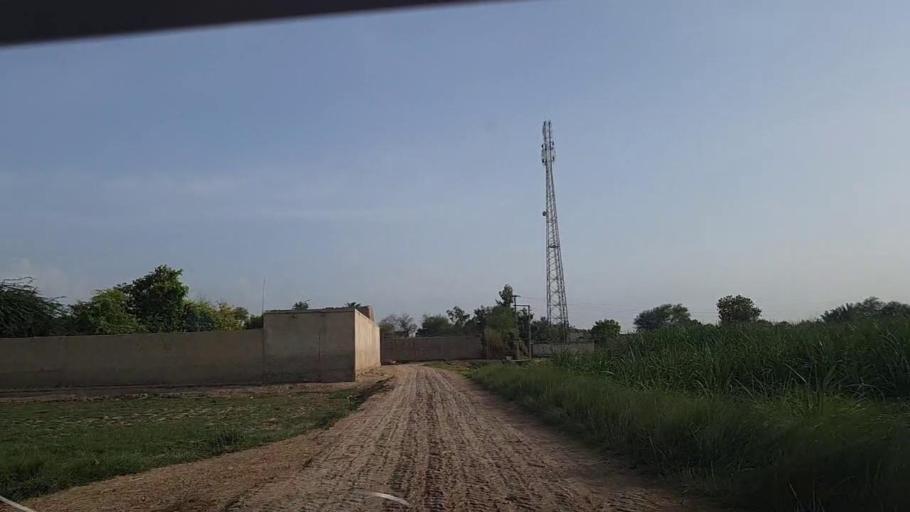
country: PK
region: Sindh
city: Ghotki
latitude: 27.9786
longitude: 69.2591
